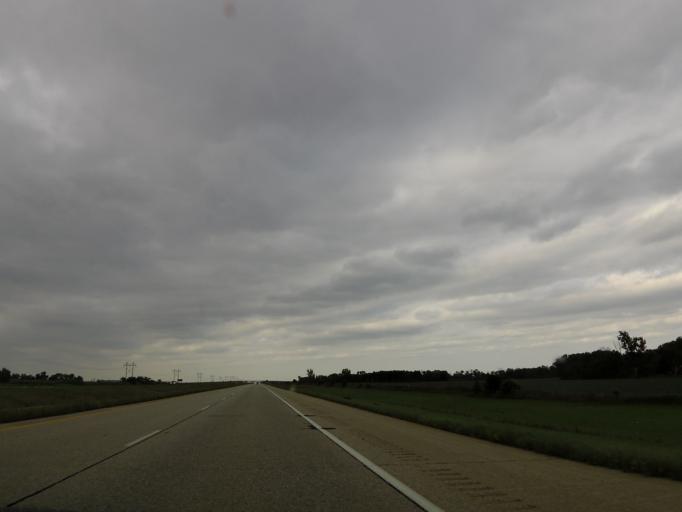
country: US
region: North Dakota
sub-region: Richland County
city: Wahpeton
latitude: 46.1377
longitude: -96.8345
